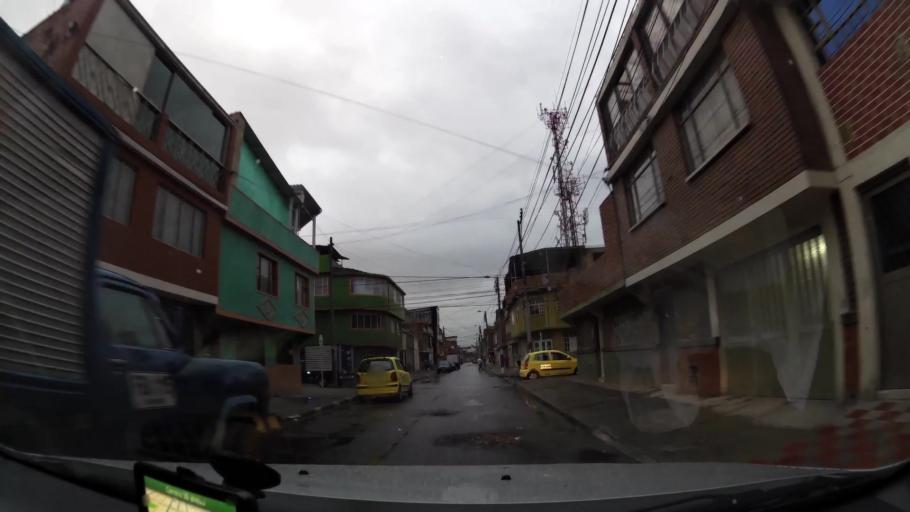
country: CO
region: Bogota D.C.
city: Bogota
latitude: 4.5876
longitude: -74.1357
